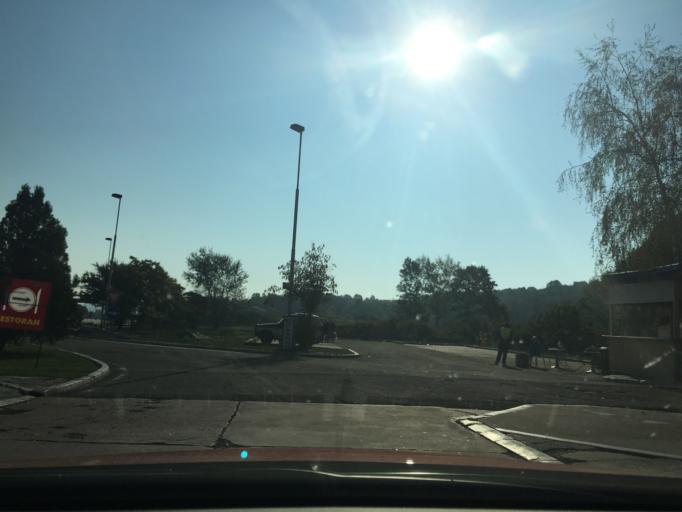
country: RS
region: Central Serbia
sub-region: Podunavski Okrug
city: Smederevo
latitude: 44.5758
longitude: 20.8924
